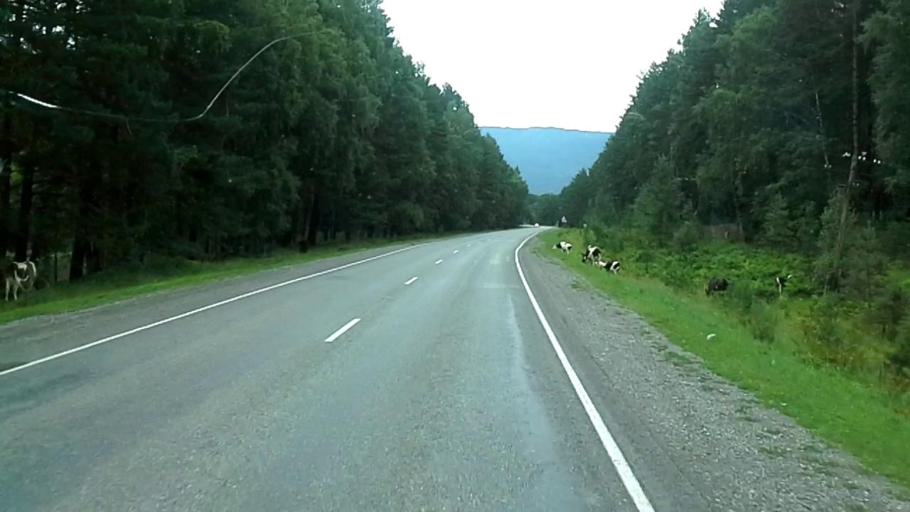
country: RU
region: Altay
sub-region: Mayminskiy Rayon
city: Manzherok
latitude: 51.8334
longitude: 85.7491
